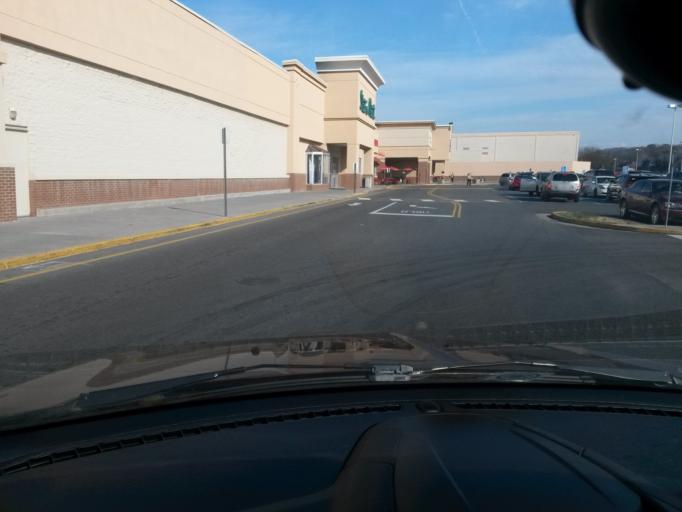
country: US
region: Virginia
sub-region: Roanoke County
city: Narrows
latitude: 37.2291
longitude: -79.9794
